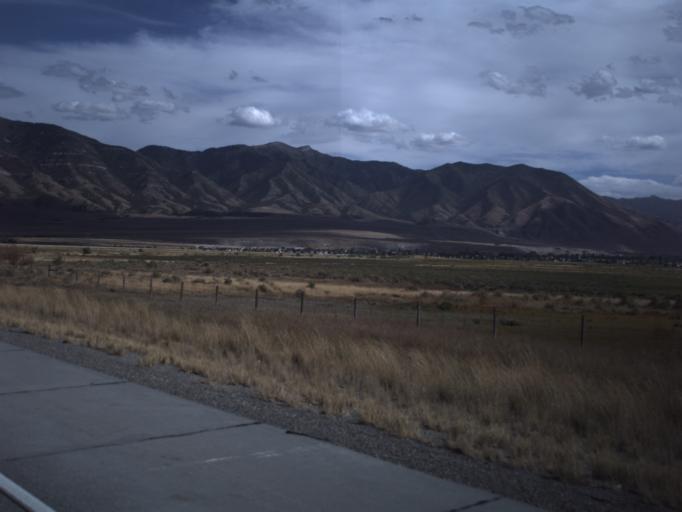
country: US
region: Utah
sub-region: Tooele County
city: Stansbury park
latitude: 40.6635
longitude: -112.3219
